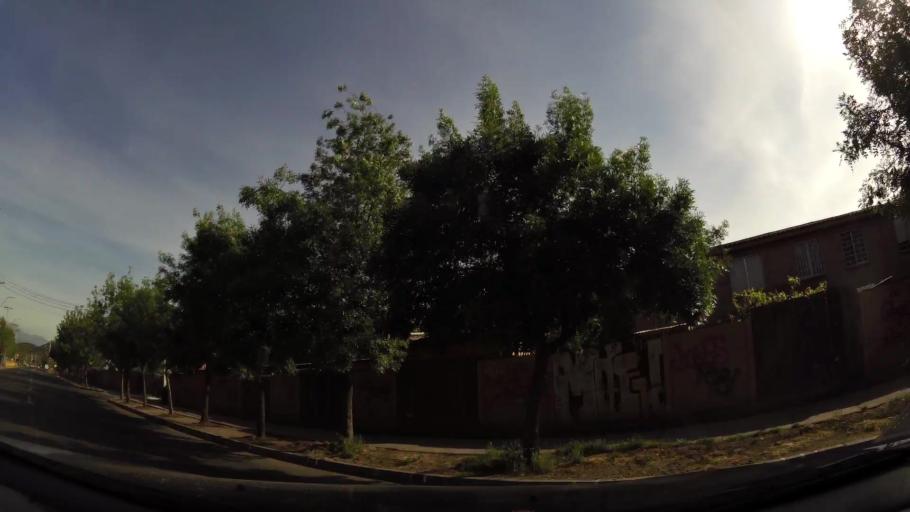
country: CL
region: Santiago Metropolitan
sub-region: Provincia de Cordillera
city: Puente Alto
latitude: -33.5860
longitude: -70.5573
